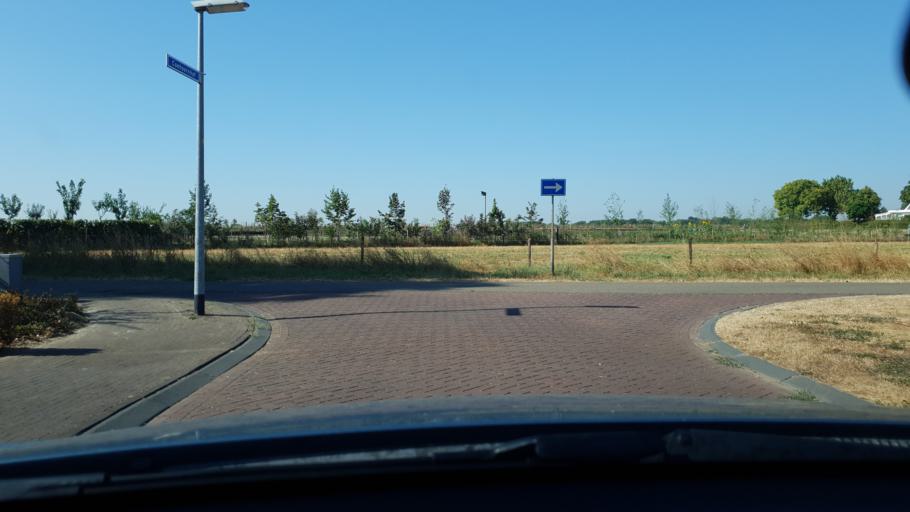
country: NL
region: North Brabant
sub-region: Gemeente Grave
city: Grave
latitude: 51.7706
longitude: 5.7489
